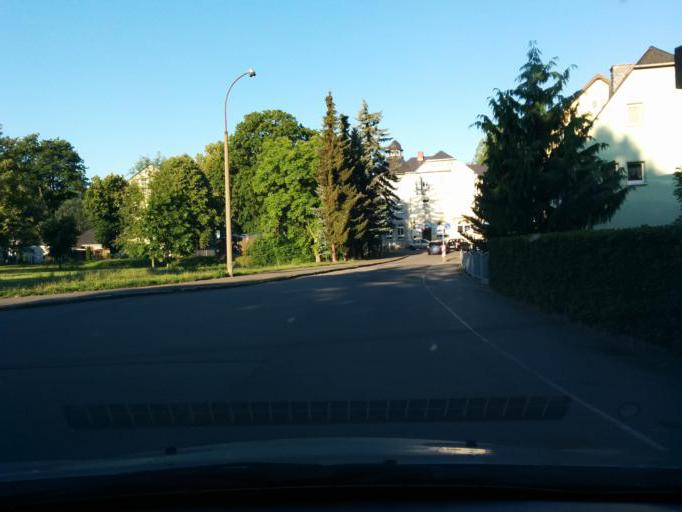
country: DE
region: Saxony
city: Floha
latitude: 50.8596
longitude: 13.0672
